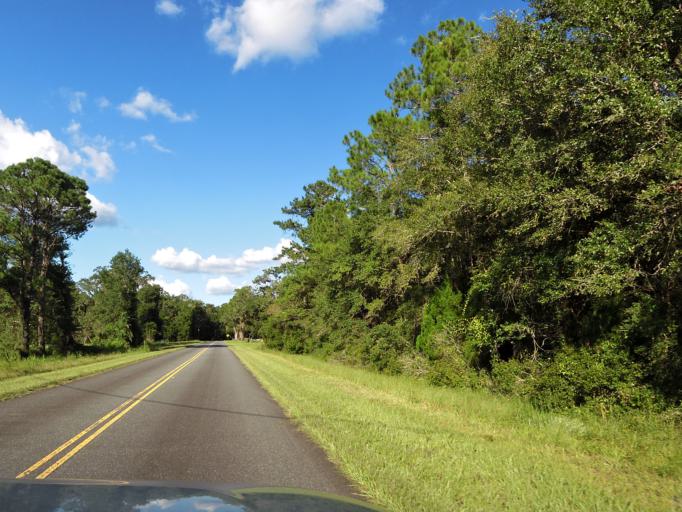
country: US
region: Florida
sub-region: Wakulla County
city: Crawfordville
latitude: 30.0648
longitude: -84.5167
